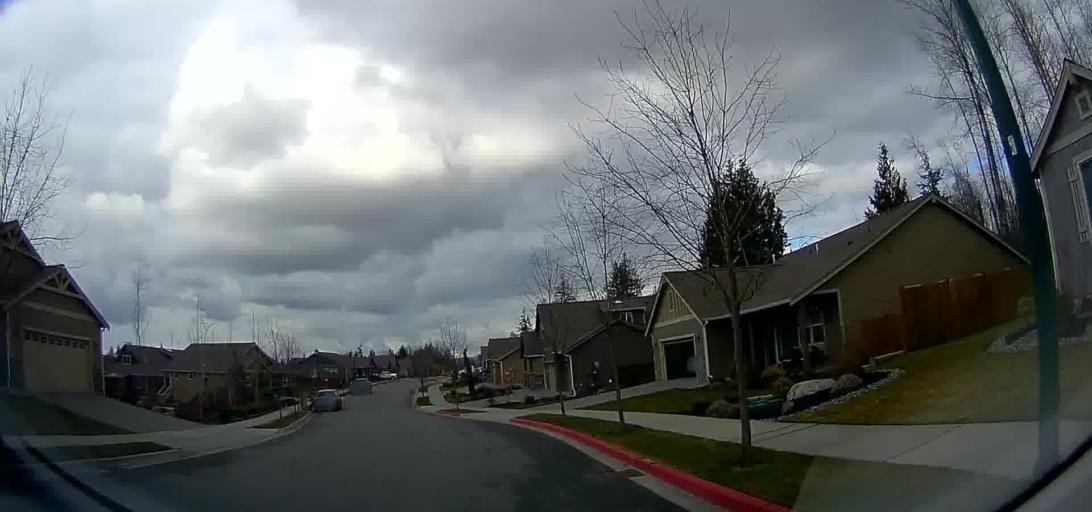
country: US
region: Washington
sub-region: Skagit County
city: Big Lake
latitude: 48.4235
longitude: -122.2816
